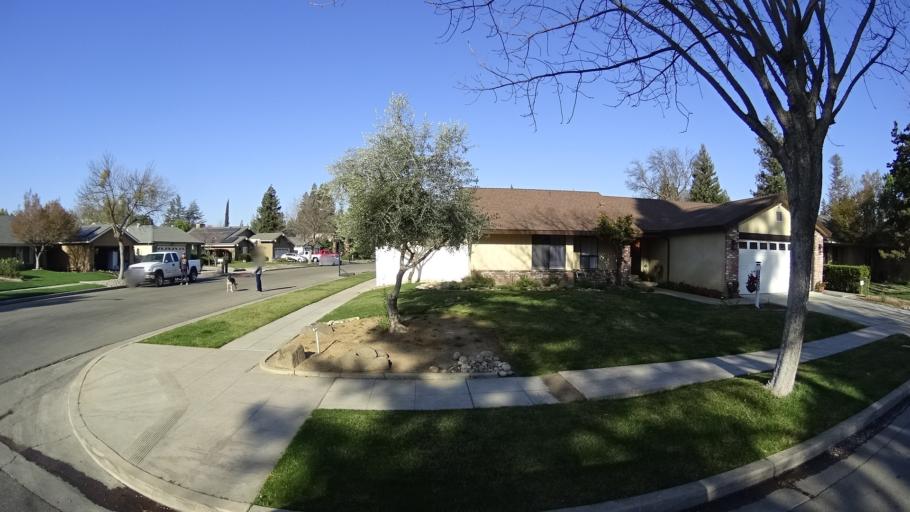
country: US
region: California
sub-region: Fresno County
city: Clovis
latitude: 36.8550
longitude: -119.7973
